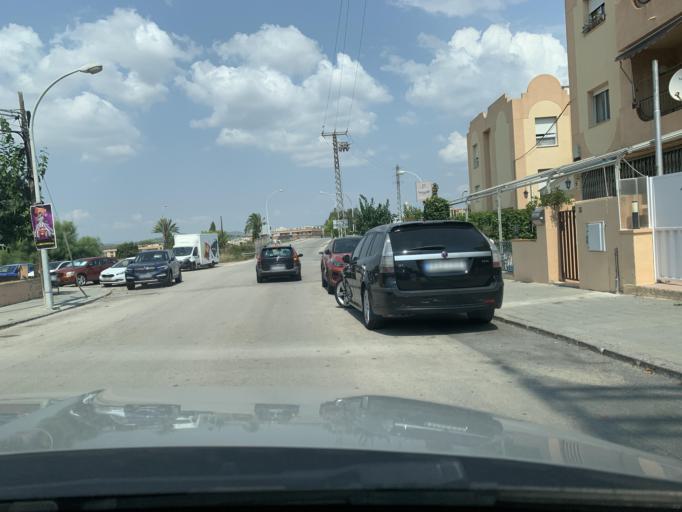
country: ES
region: Catalonia
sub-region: Provincia de Tarragona
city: Torredembarra
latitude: 41.1401
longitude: 1.3963
